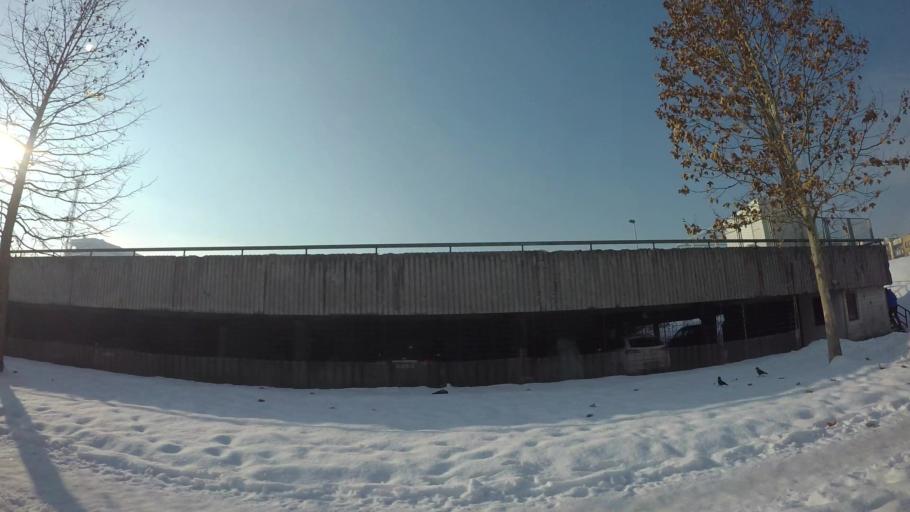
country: BA
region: Federation of Bosnia and Herzegovina
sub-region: Kanton Sarajevo
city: Sarajevo
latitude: 43.8268
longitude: 18.3558
